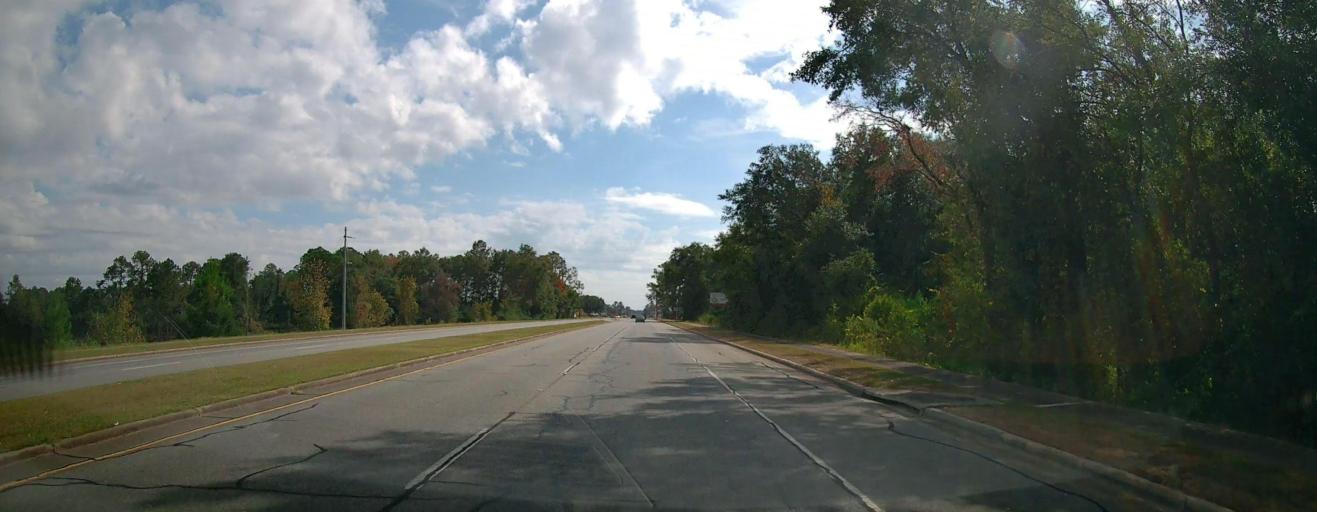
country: US
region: Georgia
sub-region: Mitchell County
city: Camilla
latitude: 31.2414
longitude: -84.2001
